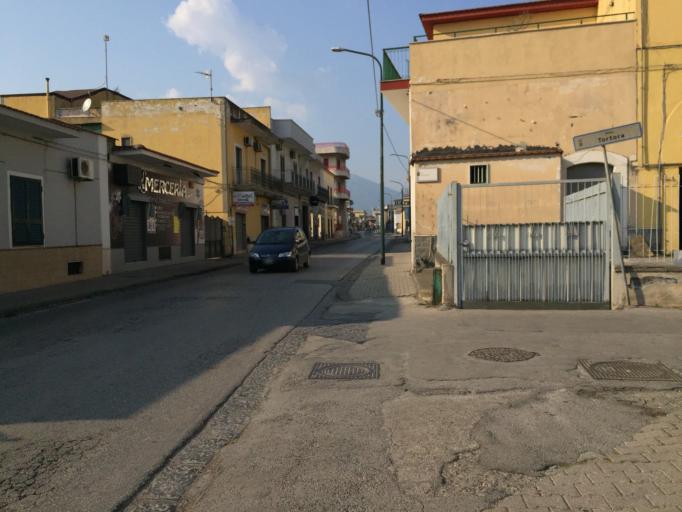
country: IT
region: Campania
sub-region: Provincia di Napoli
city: Pompei
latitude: 40.7536
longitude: 14.4991
